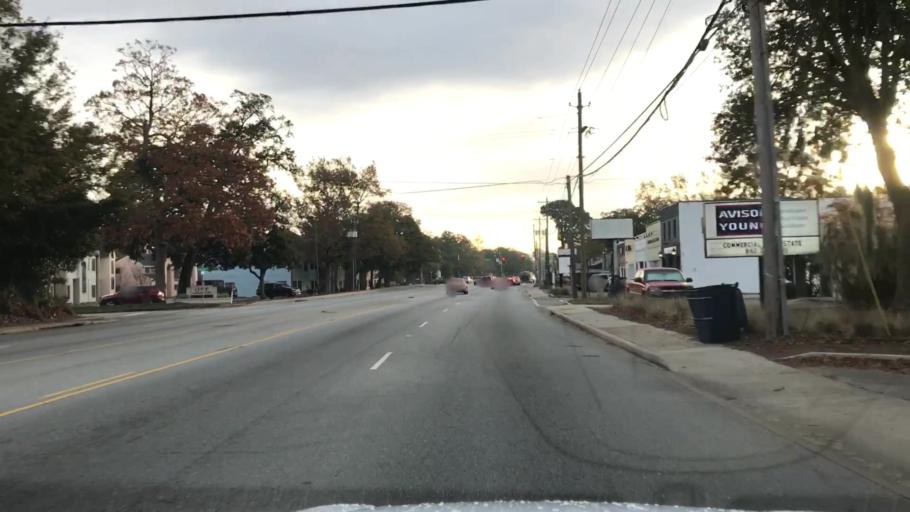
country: US
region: South Carolina
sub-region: Charleston County
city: North Charleston
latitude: 32.7974
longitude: -79.9994
